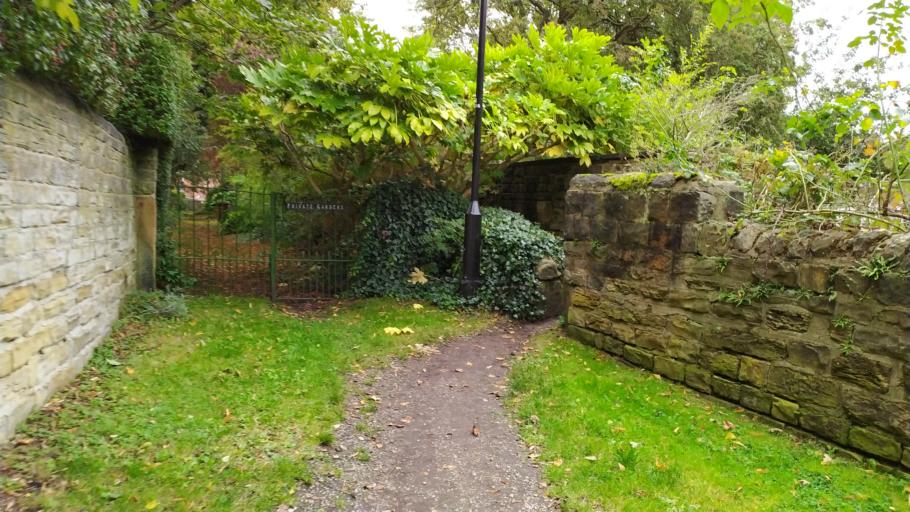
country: GB
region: England
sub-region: City and Borough of Leeds
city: Leeds
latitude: 53.8179
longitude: -1.5630
